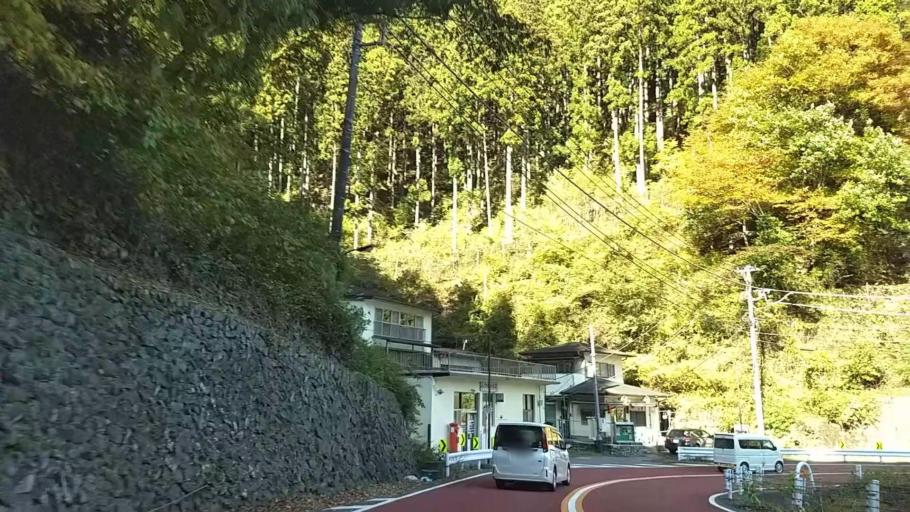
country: JP
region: Yamanashi
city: Uenohara
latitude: 35.7865
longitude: 139.0425
